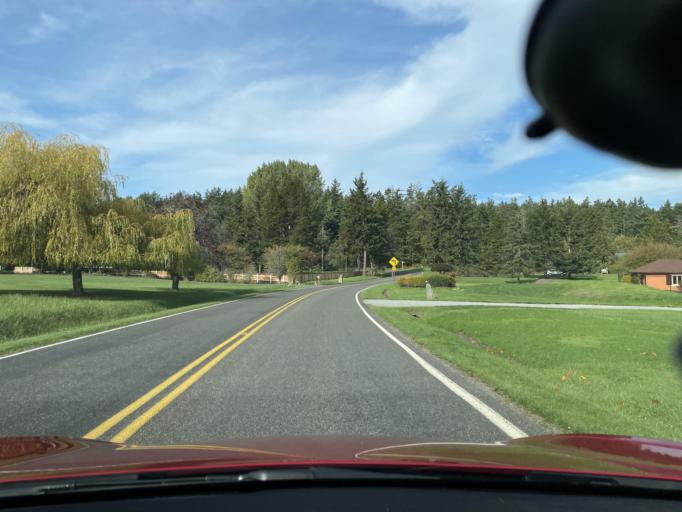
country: US
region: Washington
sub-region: San Juan County
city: Friday Harbor
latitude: 48.5275
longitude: -122.9809
